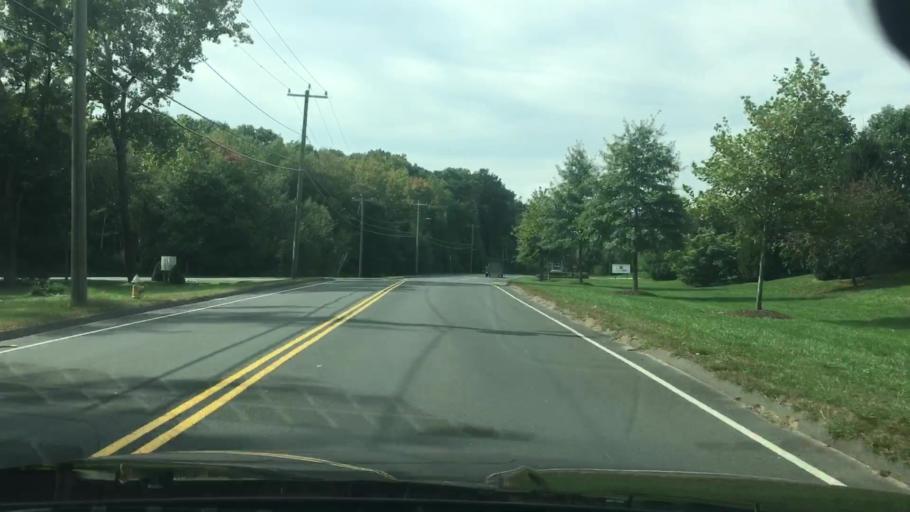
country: US
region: Connecticut
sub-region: Hartford County
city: South Windsor
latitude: 41.8593
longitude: -72.5844
